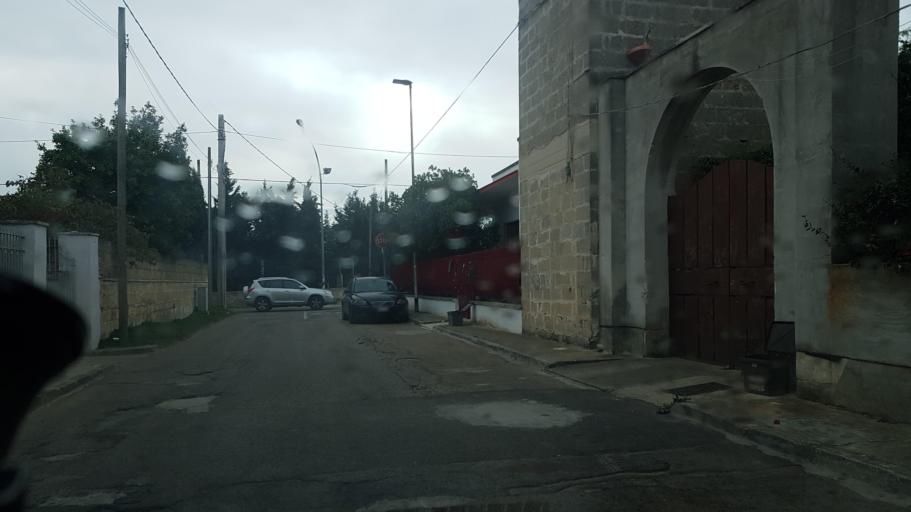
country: IT
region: Apulia
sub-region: Provincia di Lecce
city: Leverano
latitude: 40.2799
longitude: 17.9942
